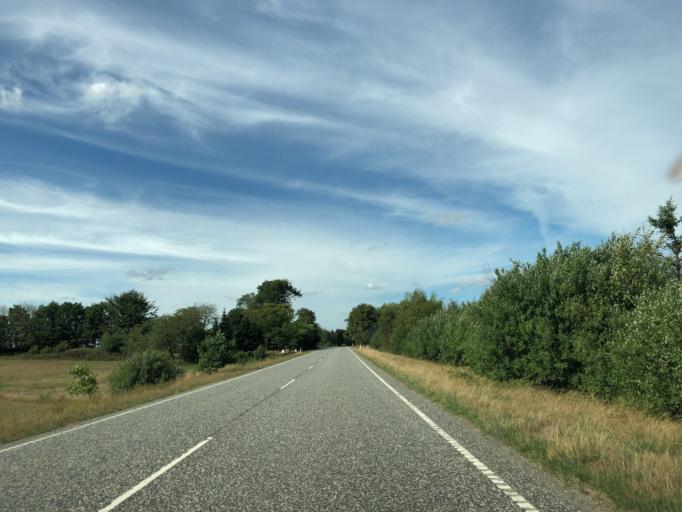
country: DK
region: Central Jutland
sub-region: Silkeborg Kommune
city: Silkeborg
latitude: 56.1436
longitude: 9.4382
